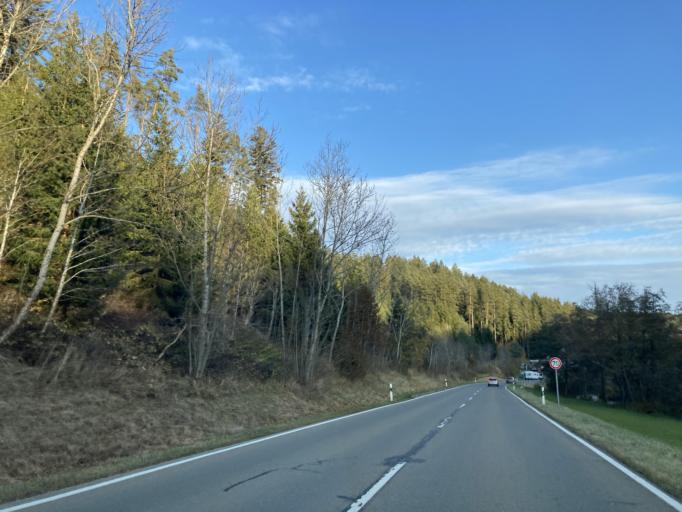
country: DE
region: Baden-Wuerttemberg
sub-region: Freiburg Region
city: Unterkirnach
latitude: 47.9903
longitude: 8.3725
